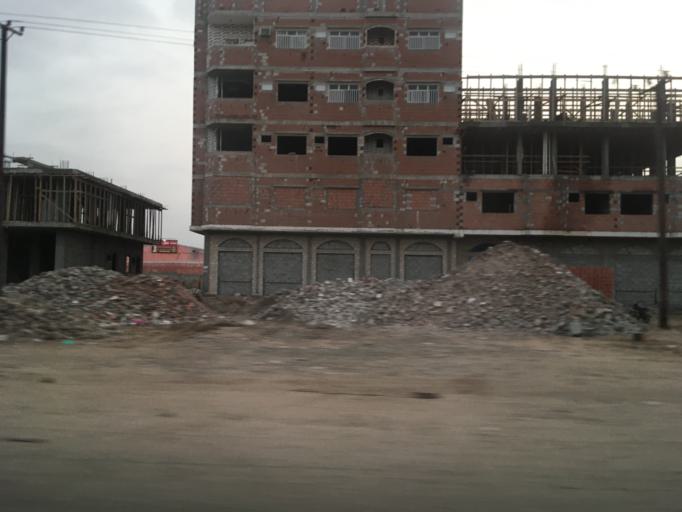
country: YE
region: Lahij
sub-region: Al  Hawtah
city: Lahij
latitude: 13.0055
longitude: 44.9109
